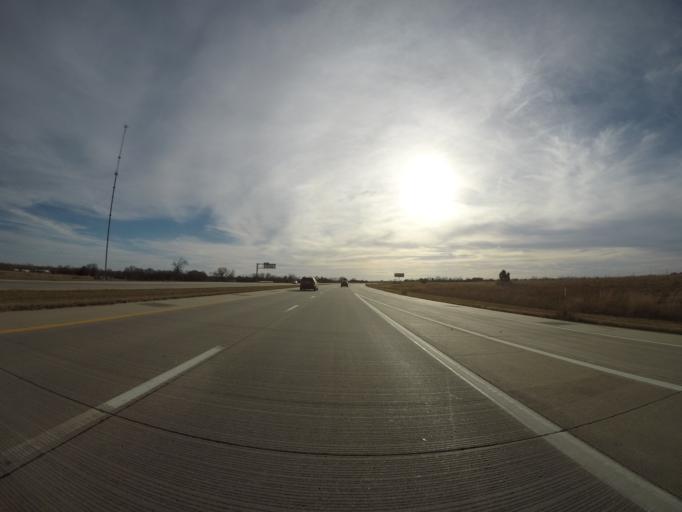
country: US
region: Kansas
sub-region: Franklin County
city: Ottawa
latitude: 38.5912
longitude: -95.2354
